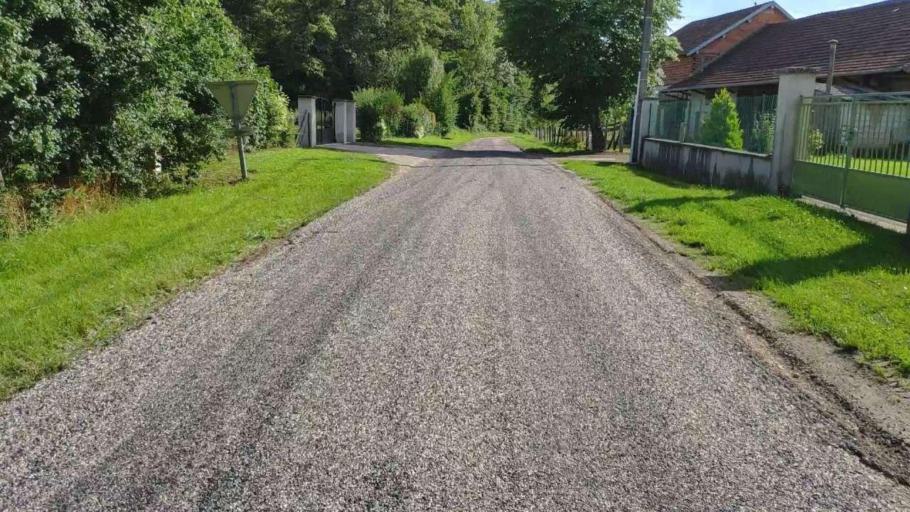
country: FR
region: Franche-Comte
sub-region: Departement du Jura
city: Bletterans
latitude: 46.8251
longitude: 5.5287
